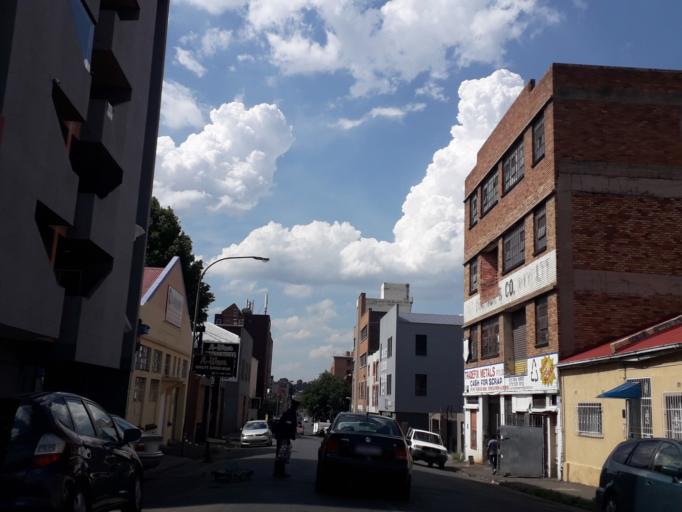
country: ZA
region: Gauteng
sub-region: City of Johannesburg Metropolitan Municipality
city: Johannesburg
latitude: -26.2086
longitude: 28.0230
